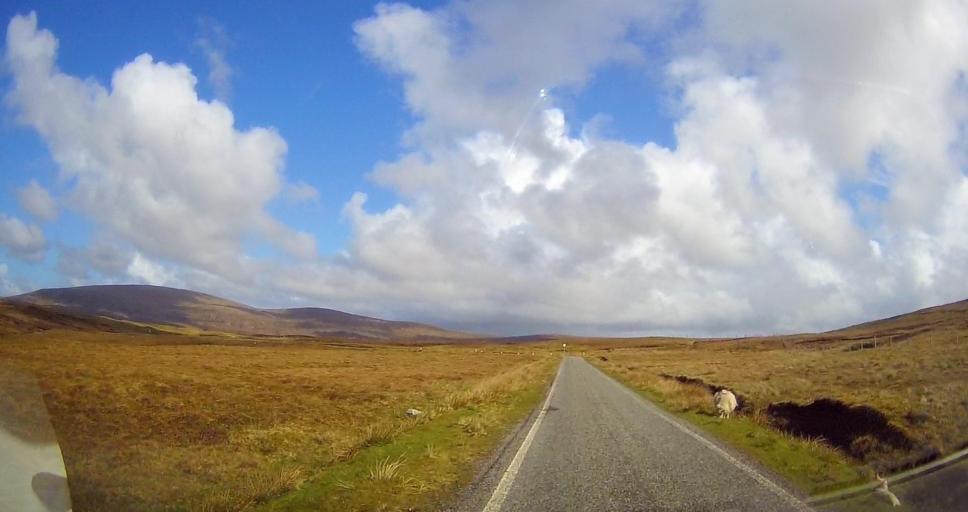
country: GB
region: Scotland
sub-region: Shetland Islands
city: Lerwick
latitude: 60.4940
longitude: -1.3916
